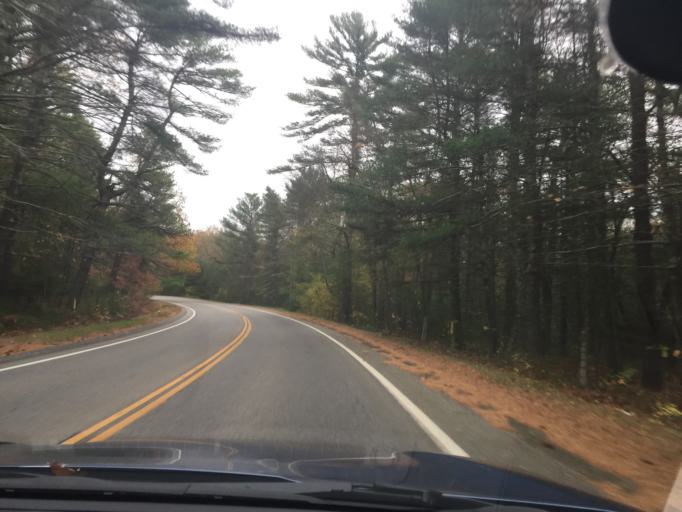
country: US
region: Rhode Island
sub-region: Providence County
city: North Scituate
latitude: 41.7839
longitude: -71.5910
